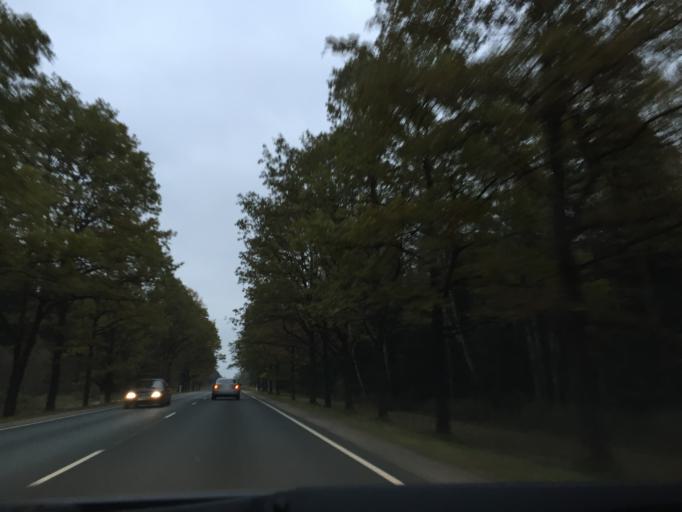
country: LV
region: Ozolnieku
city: Ozolnieki
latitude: 56.7068
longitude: 23.8217
